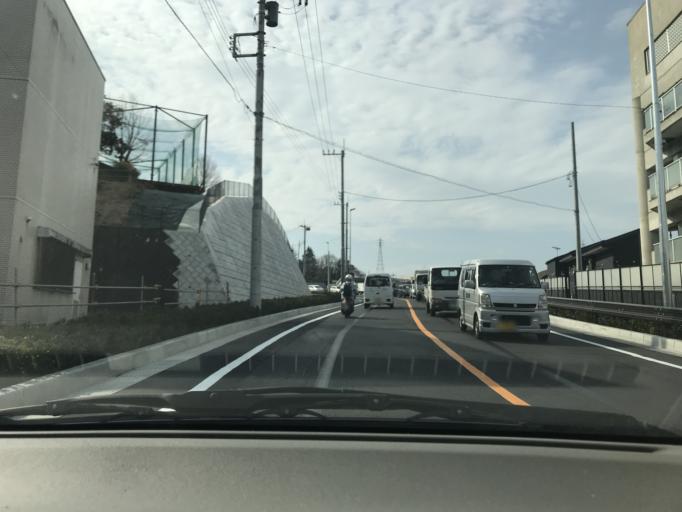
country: JP
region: Tokyo
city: Chofugaoka
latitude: 35.6108
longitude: 139.5514
